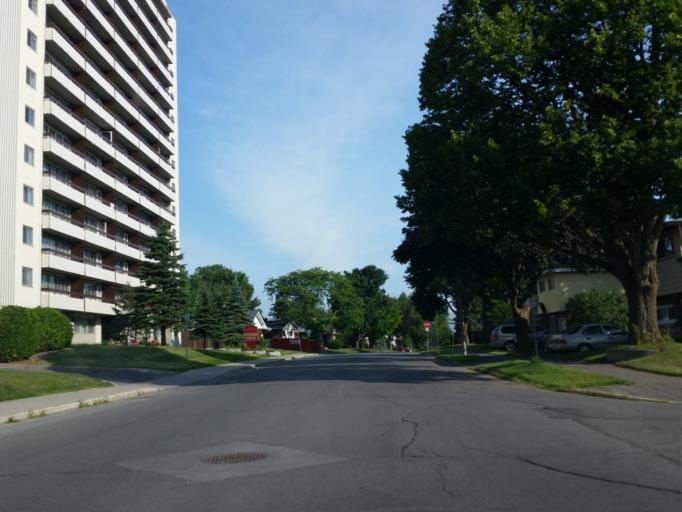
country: CA
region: Ontario
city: Ottawa
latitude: 45.3556
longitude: -75.7571
